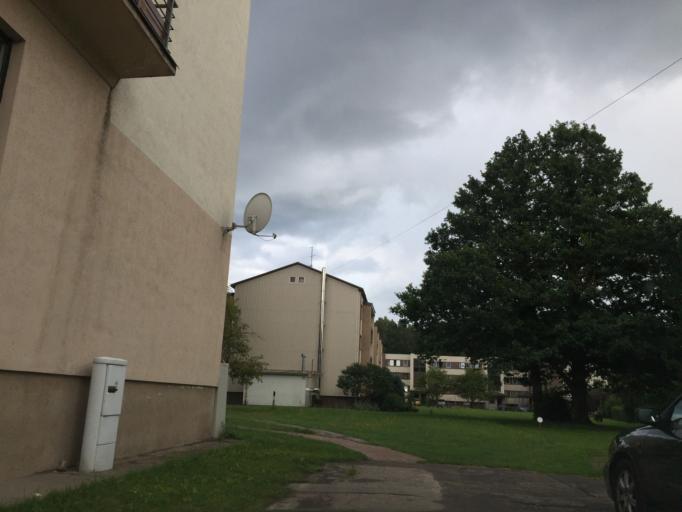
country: LV
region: Babite
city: Pinki
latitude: 56.9560
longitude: 23.9532
